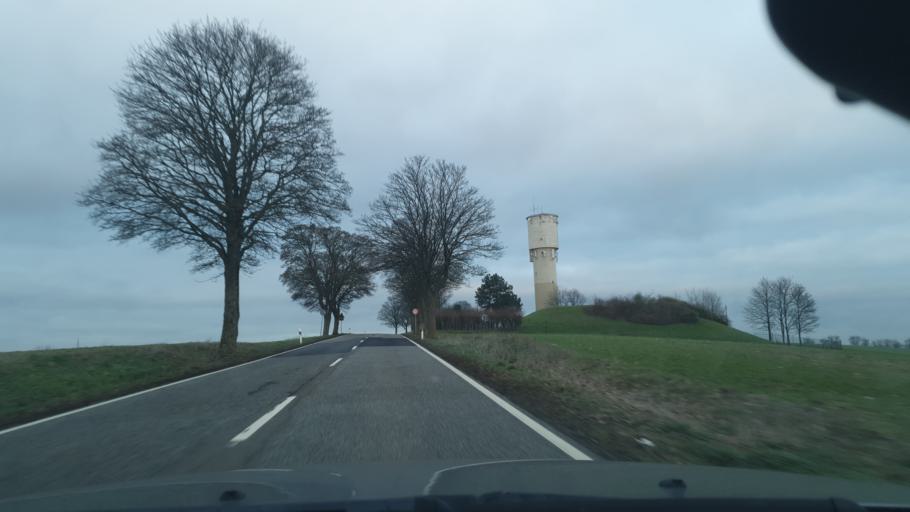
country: DE
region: Rheinland-Pfalz
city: Kashofen
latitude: 49.3200
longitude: 7.4076
